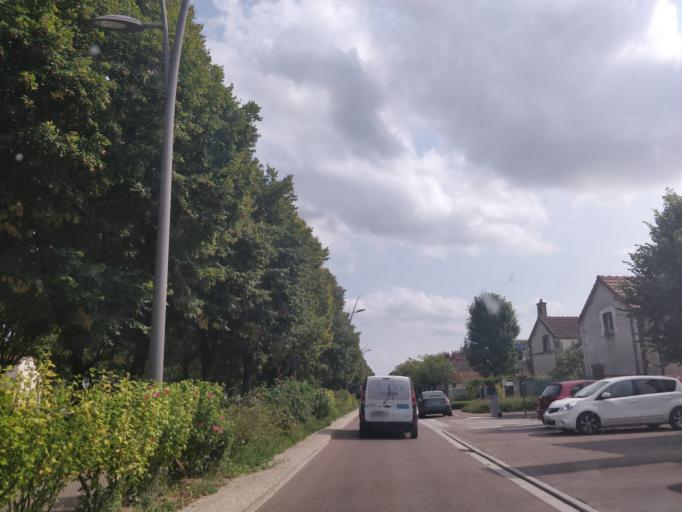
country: FR
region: Champagne-Ardenne
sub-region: Departement de l'Aube
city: Troyes
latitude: 48.2834
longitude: 4.0842
